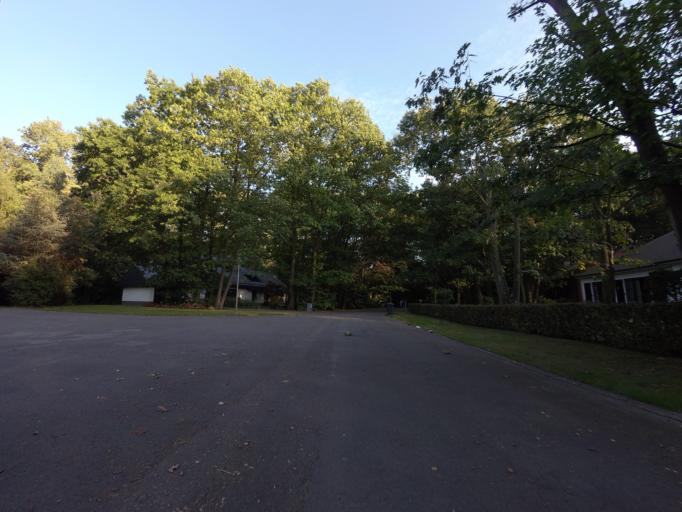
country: BE
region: Flanders
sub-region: Provincie Vlaams-Brabant
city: Boortmeerbeek
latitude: 50.9551
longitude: 4.5798
